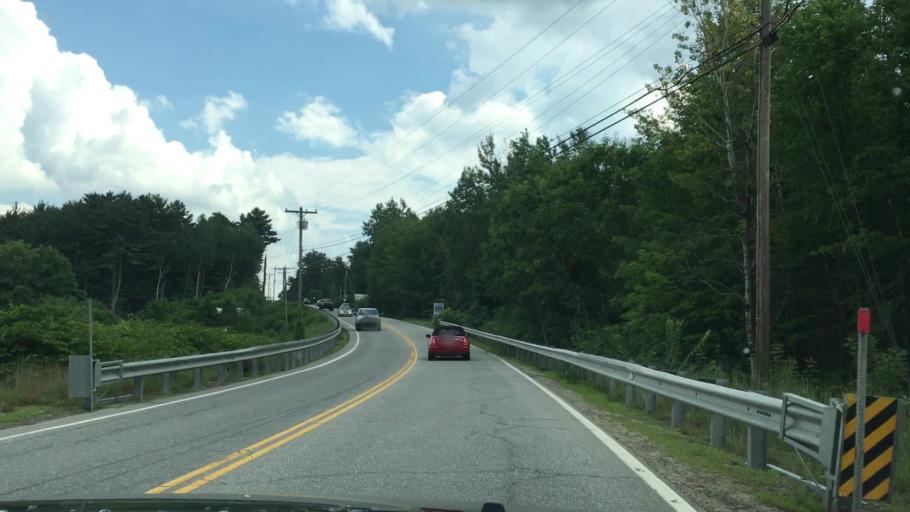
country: US
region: New Hampshire
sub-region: Belknap County
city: Meredith
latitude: 43.6284
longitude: -71.4871
